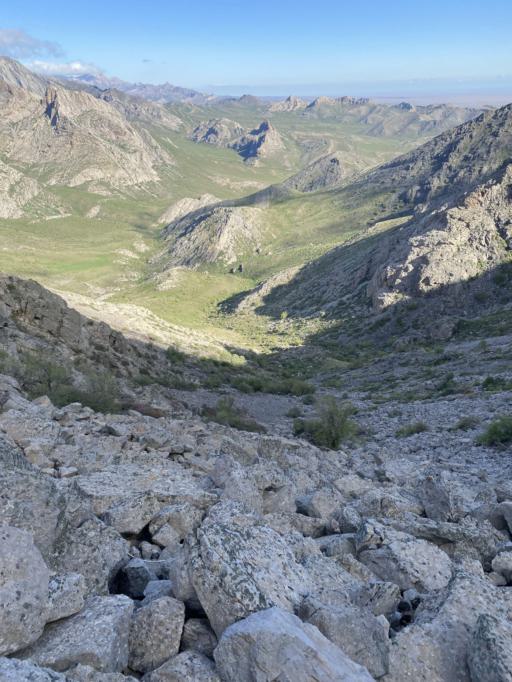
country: KZ
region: Ongtustik Qazaqstan
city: Ashchysay
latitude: 43.6380
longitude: 68.9541
